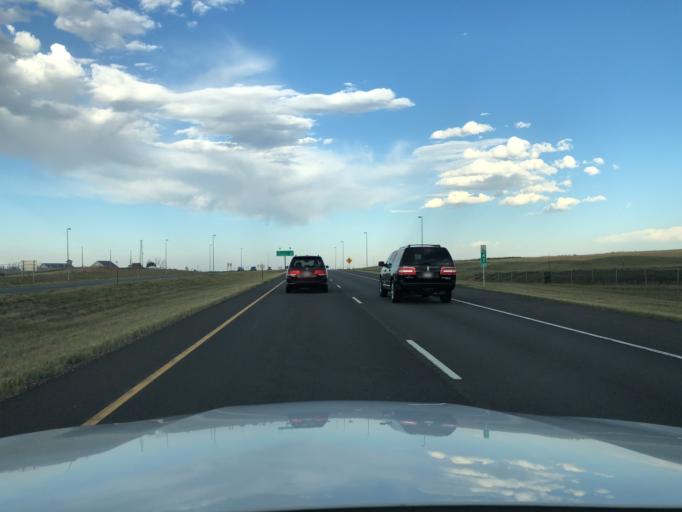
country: US
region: Colorado
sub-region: Boulder County
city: Erie
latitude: 39.9844
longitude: -105.0142
